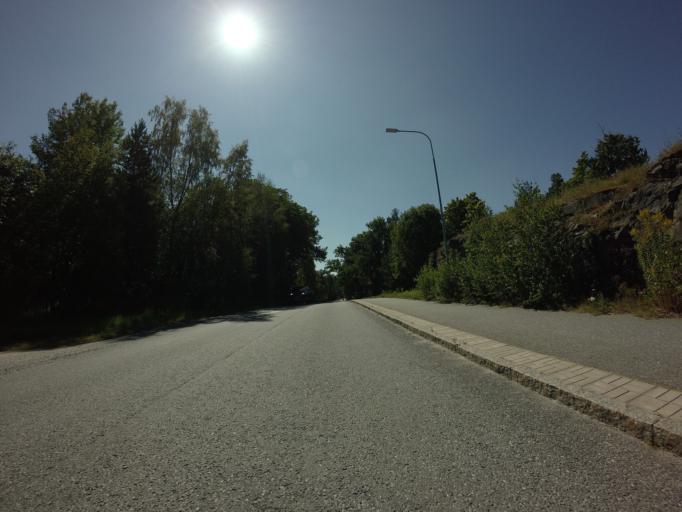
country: SE
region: Stockholm
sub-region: Lidingo
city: Brevik
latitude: 59.3589
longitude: 18.2233
